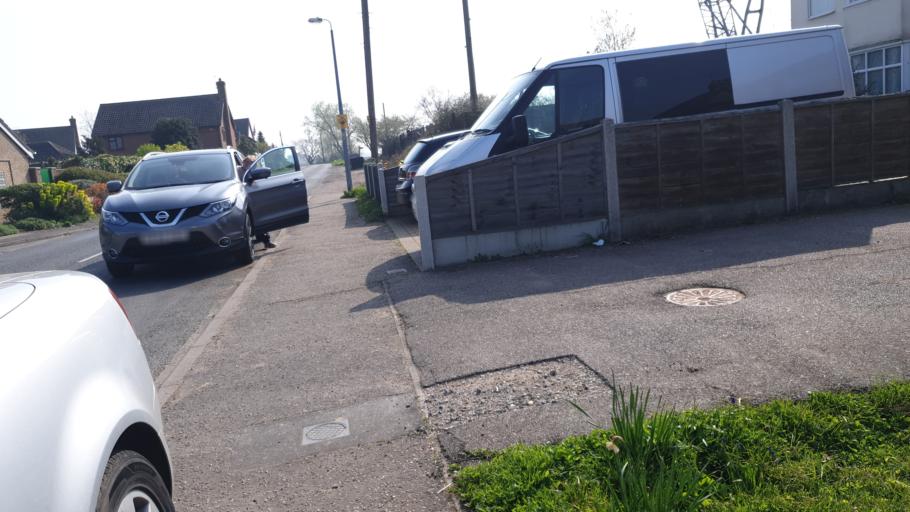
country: GB
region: England
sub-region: Essex
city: Mistley
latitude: 51.9111
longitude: 1.1429
